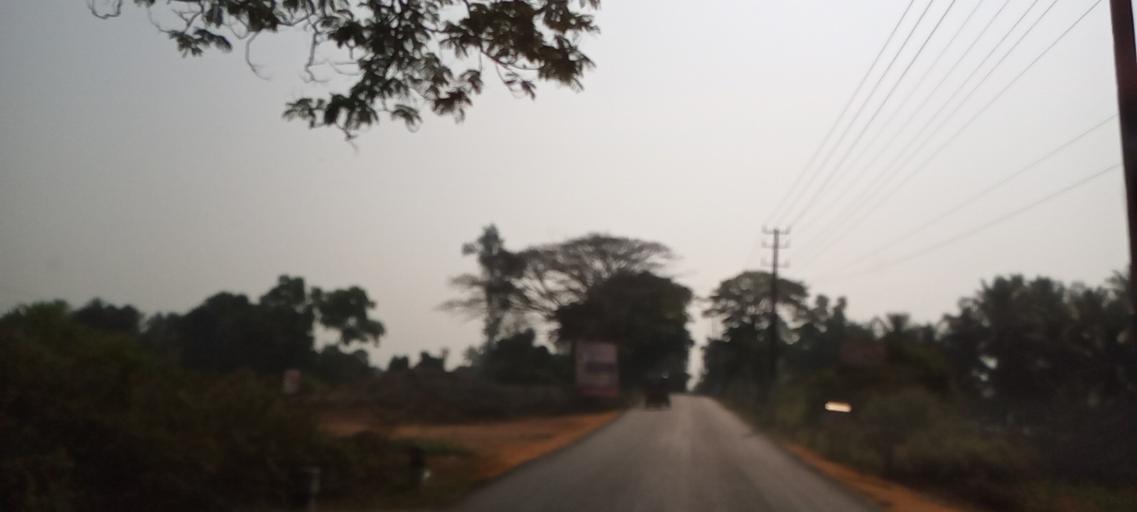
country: IN
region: Karnataka
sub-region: Udupi
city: Coondapoor
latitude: 13.5083
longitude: 74.7206
